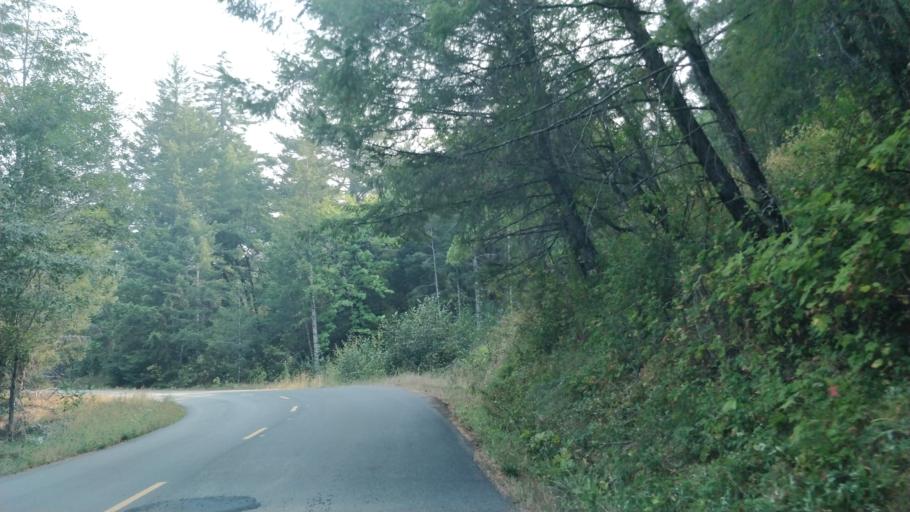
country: US
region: California
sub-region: Humboldt County
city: Rio Dell
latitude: 40.3040
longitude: -124.2564
